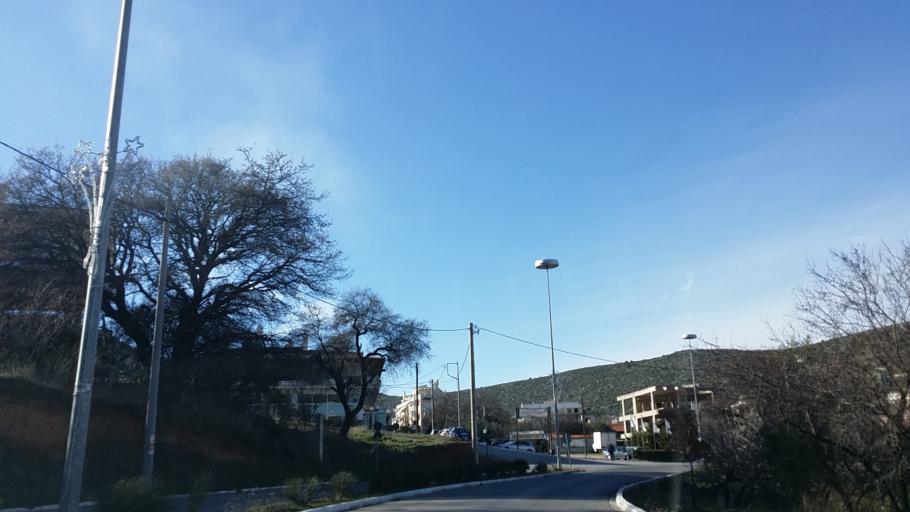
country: GR
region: Attica
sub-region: Nomarchia Dytikis Attikis
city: Fyli
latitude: 38.0985
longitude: 23.6699
